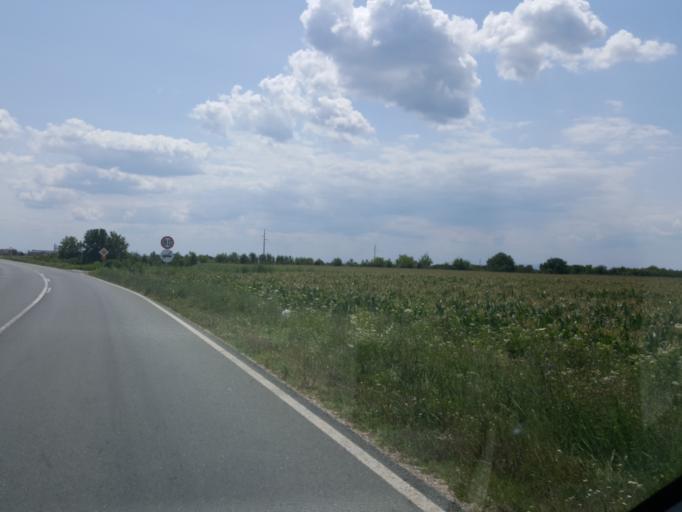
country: RS
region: Autonomna Pokrajina Vojvodina
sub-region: Sremski Okrug
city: Pecinci
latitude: 44.9158
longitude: 19.9566
